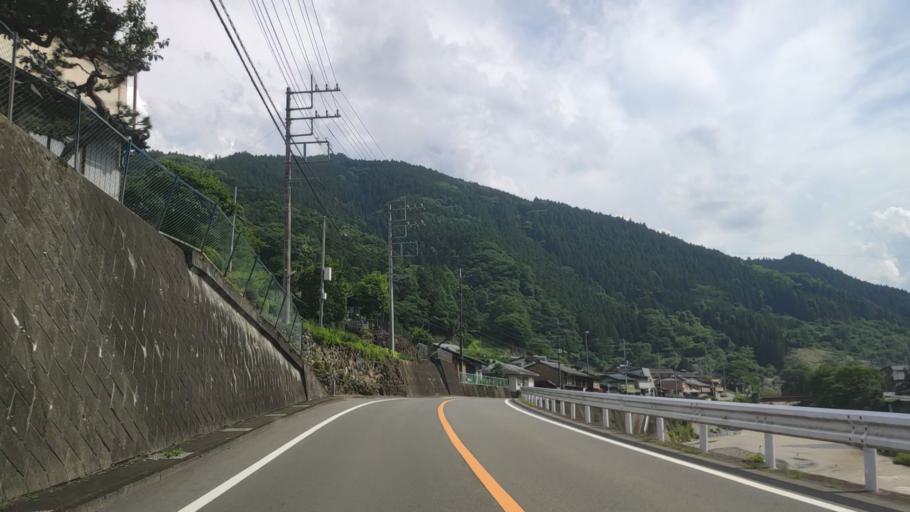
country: JP
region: Gunma
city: Tomioka
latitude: 36.1826
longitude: 138.7453
